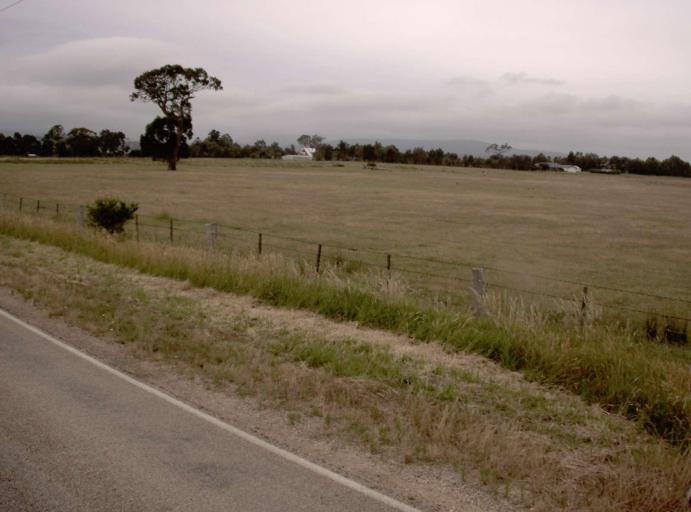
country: AU
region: Victoria
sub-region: East Gippsland
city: Bairnsdale
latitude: -37.8058
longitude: 147.4385
